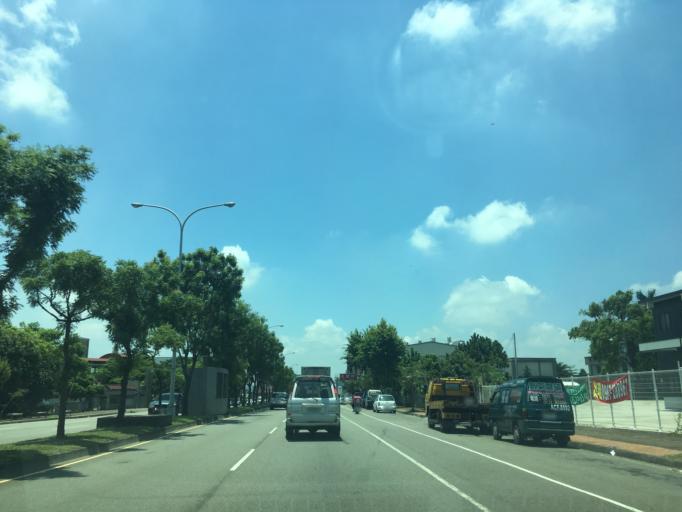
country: TW
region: Taiwan
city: Fengyuan
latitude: 24.2411
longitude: 120.7031
